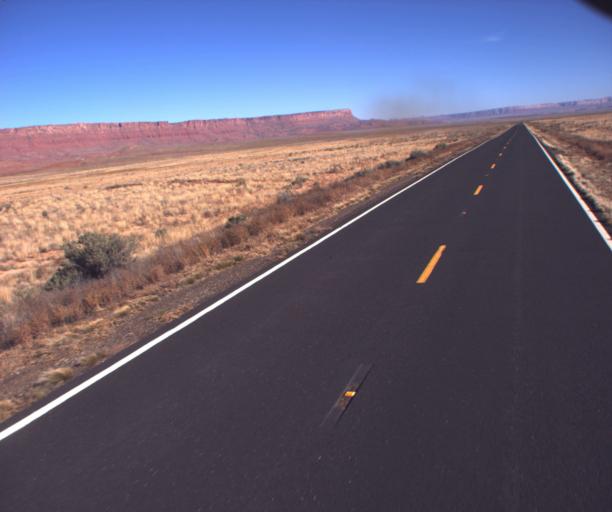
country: US
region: Arizona
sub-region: Coconino County
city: Fredonia
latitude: 36.7255
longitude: -112.0274
